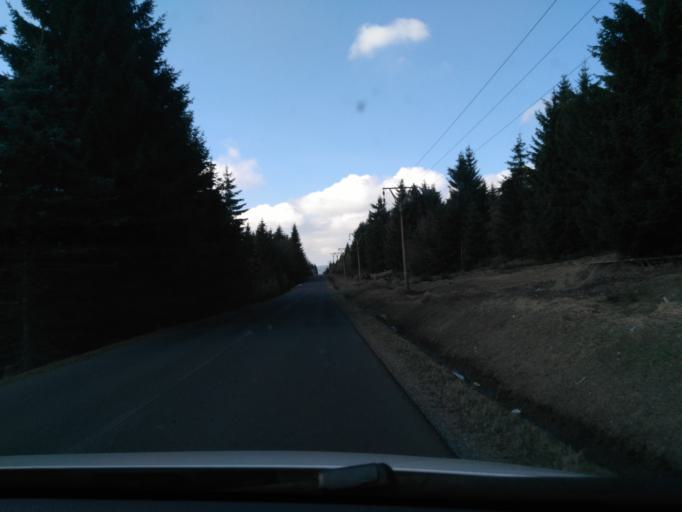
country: CZ
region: Ustecky
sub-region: Okres Chomutov
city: Kovarska
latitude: 50.4547
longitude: 13.0818
